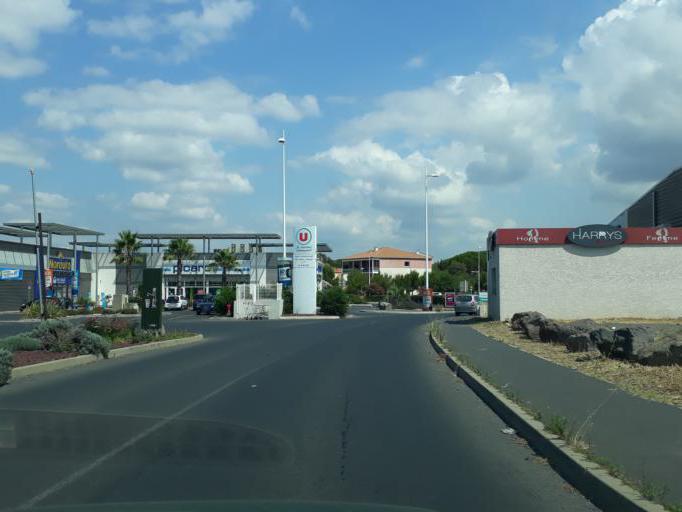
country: FR
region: Languedoc-Roussillon
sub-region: Departement de l'Herault
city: Agde
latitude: 43.2992
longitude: 3.4718
